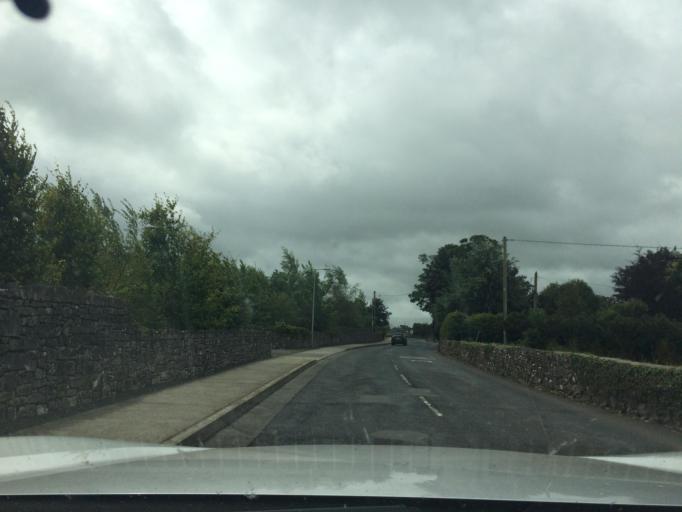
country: IE
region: Munster
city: Thurles
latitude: 52.6360
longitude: -7.8678
